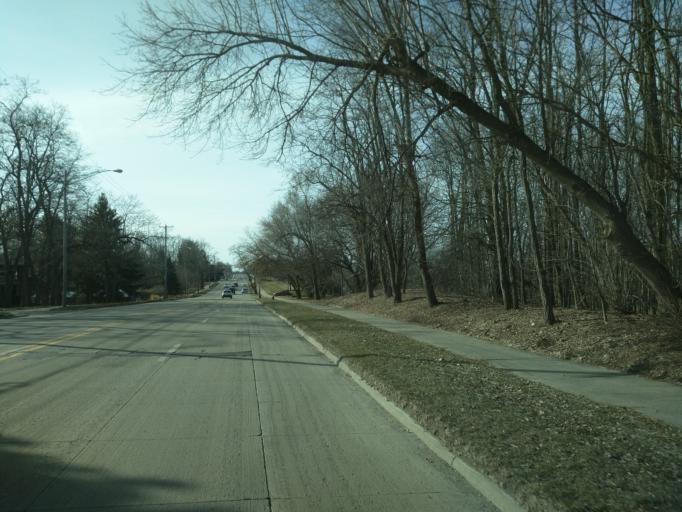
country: US
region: Michigan
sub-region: Ingham County
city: Haslett
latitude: 42.7522
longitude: -84.4086
